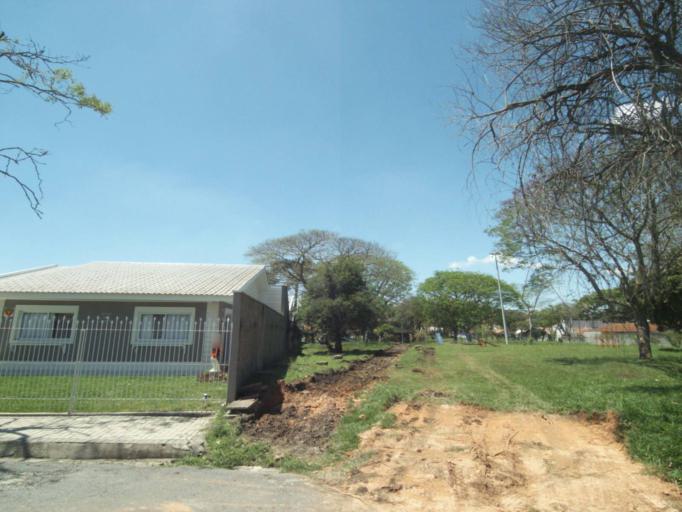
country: BR
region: Parana
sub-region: Pinhais
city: Pinhais
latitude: -25.3972
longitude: -49.2219
